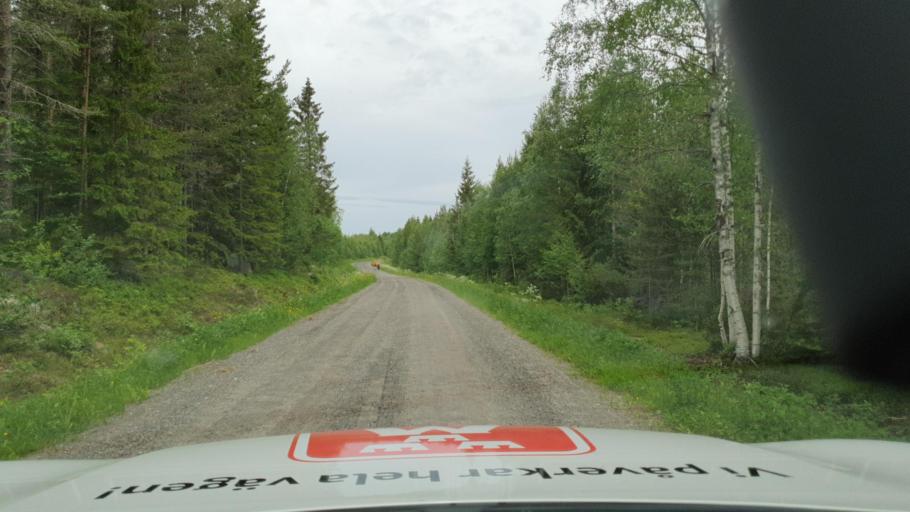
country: SE
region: Vaesterbotten
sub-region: Robertsfors Kommun
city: Robertsfors
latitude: 64.1947
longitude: 20.7133
